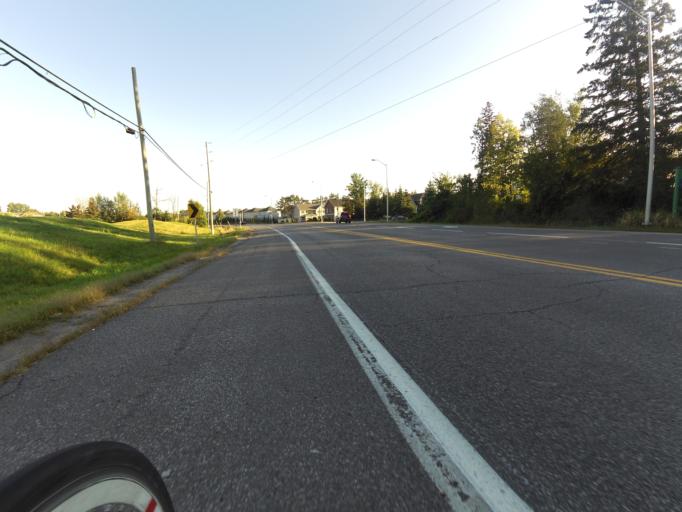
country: CA
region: Ontario
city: Bells Corners
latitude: 45.2541
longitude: -75.7261
